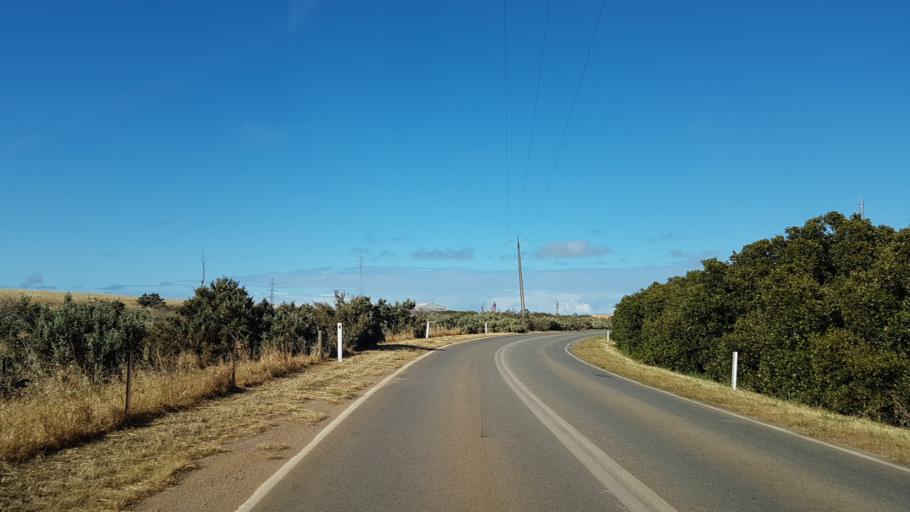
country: AU
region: South Australia
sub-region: Port Adelaide Enfield
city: Birkenhead
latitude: -34.8087
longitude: 138.5282
